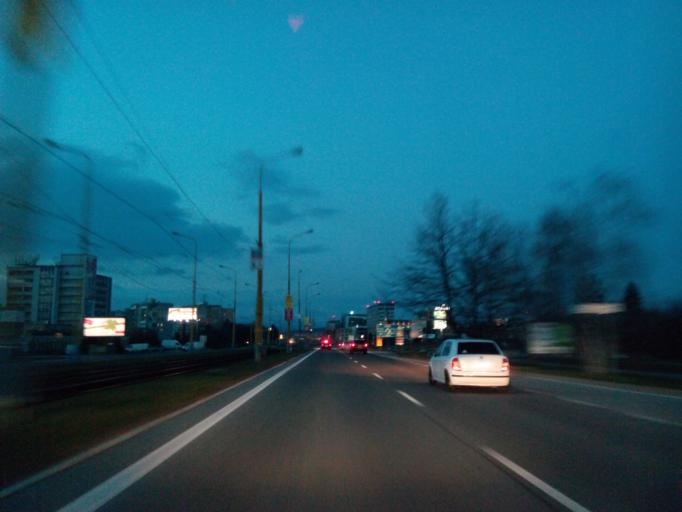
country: SK
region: Kosicky
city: Kosice
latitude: 48.7025
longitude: 21.2410
